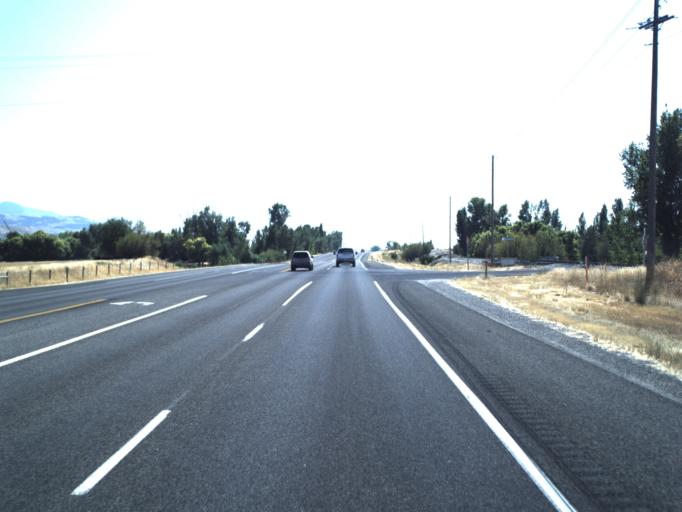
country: US
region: Utah
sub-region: Cache County
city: Richmond
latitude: 41.9596
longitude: -111.8130
